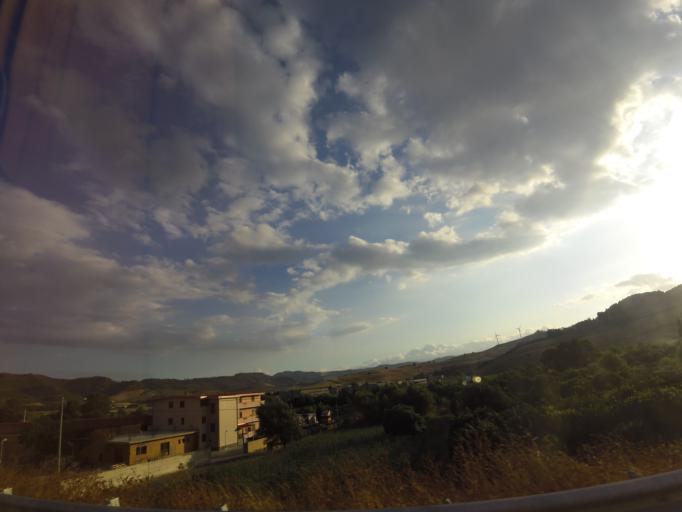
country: IT
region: Calabria
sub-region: Provincia di Catanzaro
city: Catanzaro
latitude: 38.8709
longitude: 16.5612
